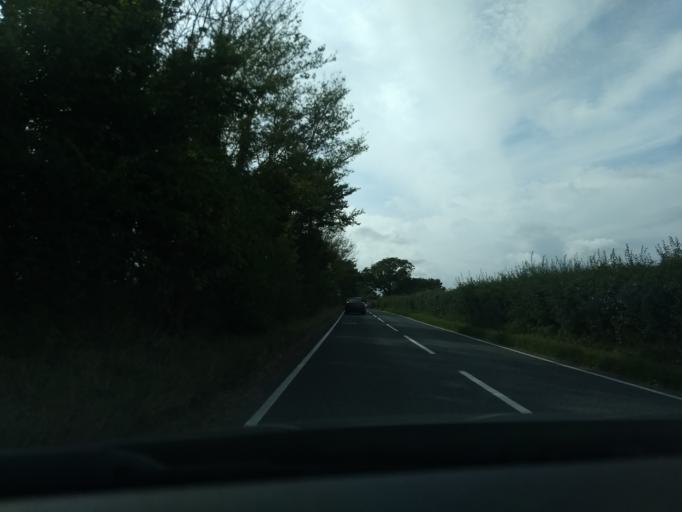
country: GB
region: England
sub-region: Suffolk
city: Ipswich
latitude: 52.0052
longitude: 1.1682
